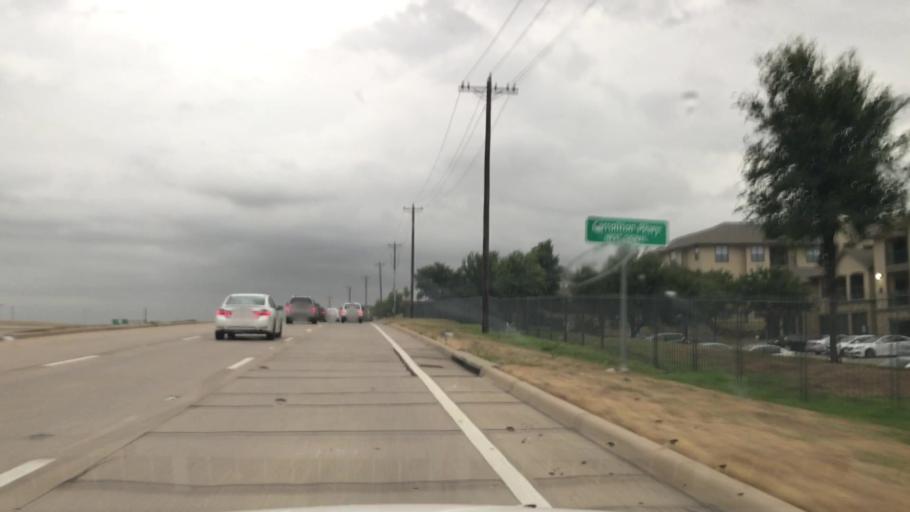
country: US
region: Texas
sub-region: Denton County
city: Lewisville
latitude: 33.0290
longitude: -96.9287
